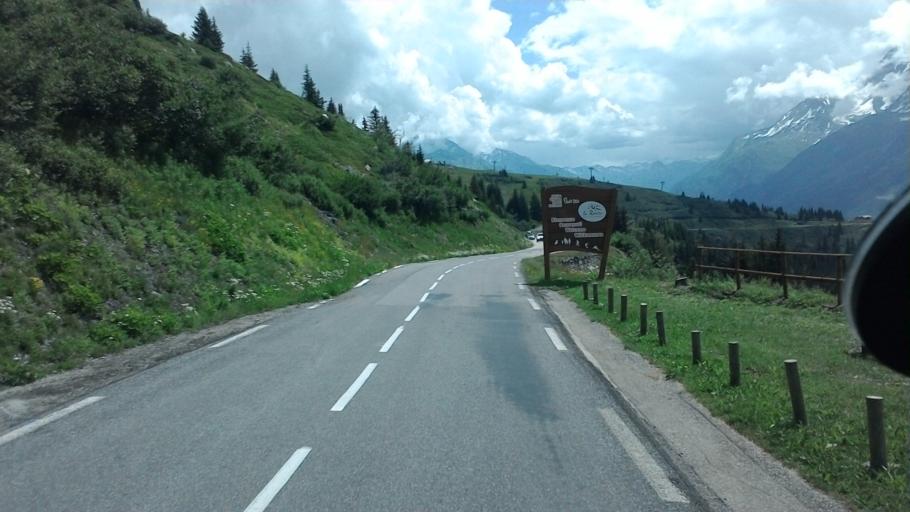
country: FR
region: Rhone-Alpes
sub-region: Departement de la Savoie
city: Seez
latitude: 45.6410
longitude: 6.8448
